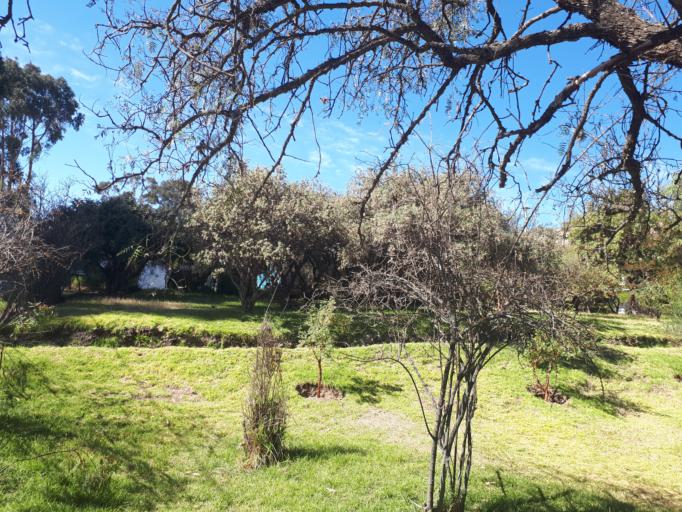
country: BO
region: La Paz
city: La Paz
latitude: -16.5379
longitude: -68.0690
